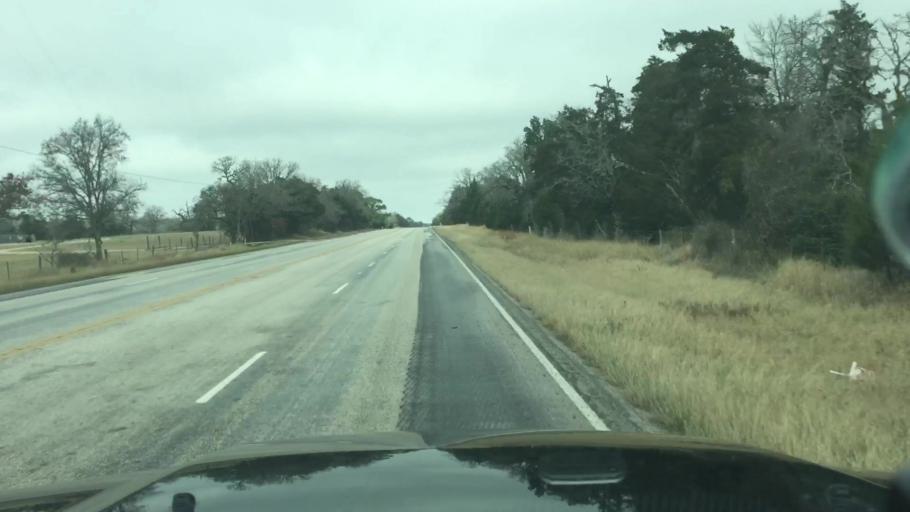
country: US
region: Texas
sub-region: Lee County
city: Giddings
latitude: 30.1077
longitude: -96.9147
